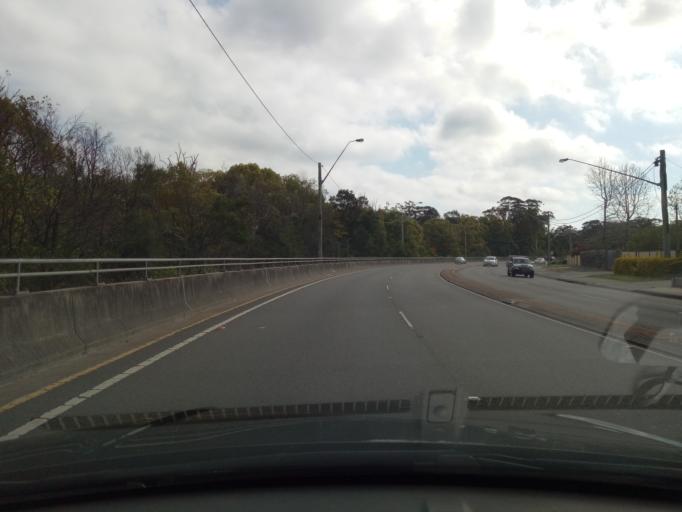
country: AU
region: New South Wales
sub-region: Gosford Shire
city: Erina
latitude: -33.4299
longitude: 151.3922
